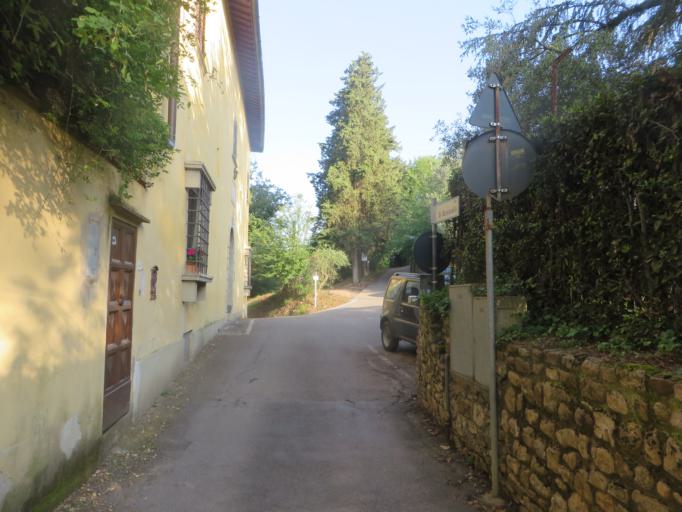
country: IT
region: Tuscany
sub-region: Province of Florence
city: Bagno a Ripoli
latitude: 43.7480
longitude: 11.3216
